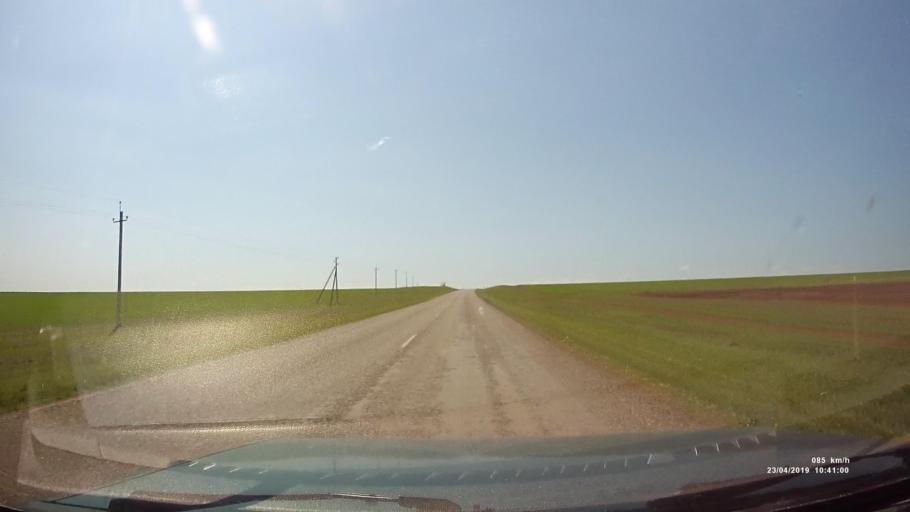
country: RU
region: Kalmykiya
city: Yashalta
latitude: 46.4991
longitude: 42.6384
